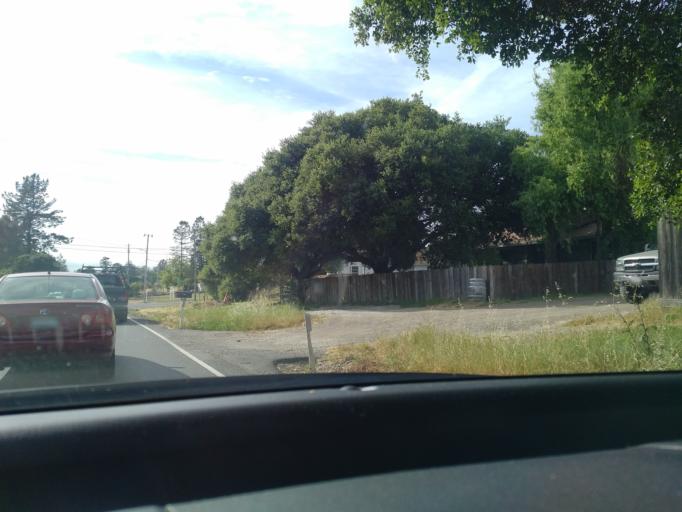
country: US
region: California
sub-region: Sonoma County
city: Penngrove
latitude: 38.2969
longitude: -122.6588
